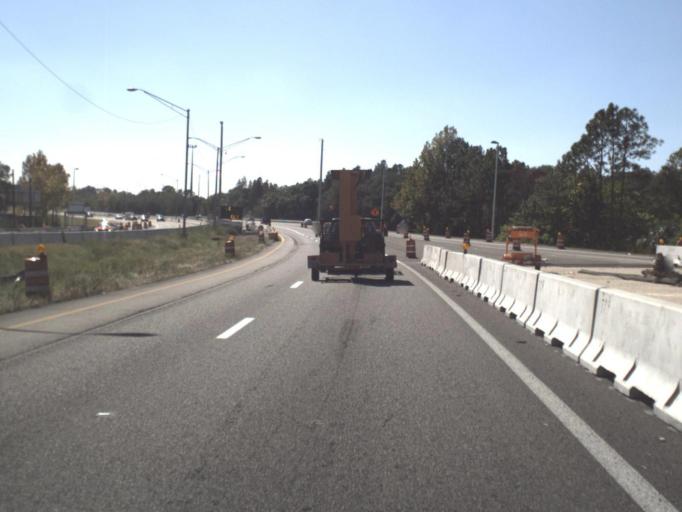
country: US
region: Florida
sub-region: Hillsborough County
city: Citrus Park
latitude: 28.0639
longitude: -82.5688
